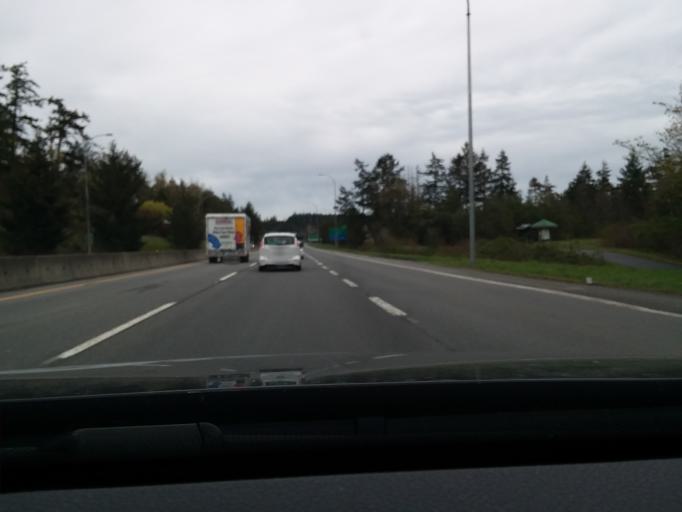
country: CA
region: British Columbia
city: North Saanich
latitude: 48.6766
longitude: -123.4258
